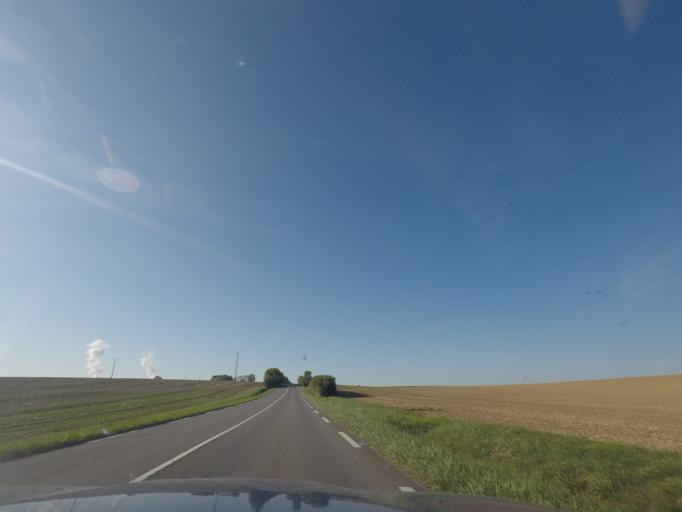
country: LU
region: Luxembourg
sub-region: Canton d'Esch-sur-Alzette
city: Frisange
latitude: 49.4845
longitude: 6.1907
